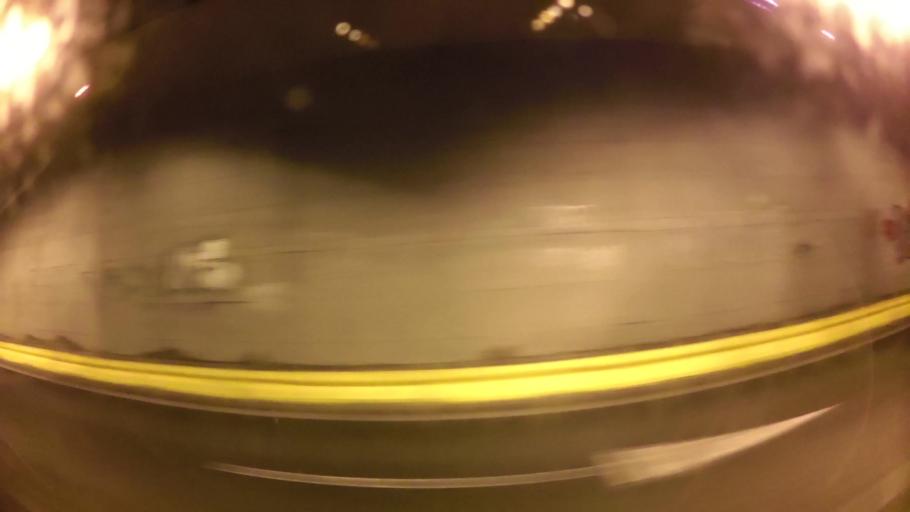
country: GR
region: Attica
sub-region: Nomos Piraios
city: Drapetsona
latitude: 37.9456
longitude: 23.6203
